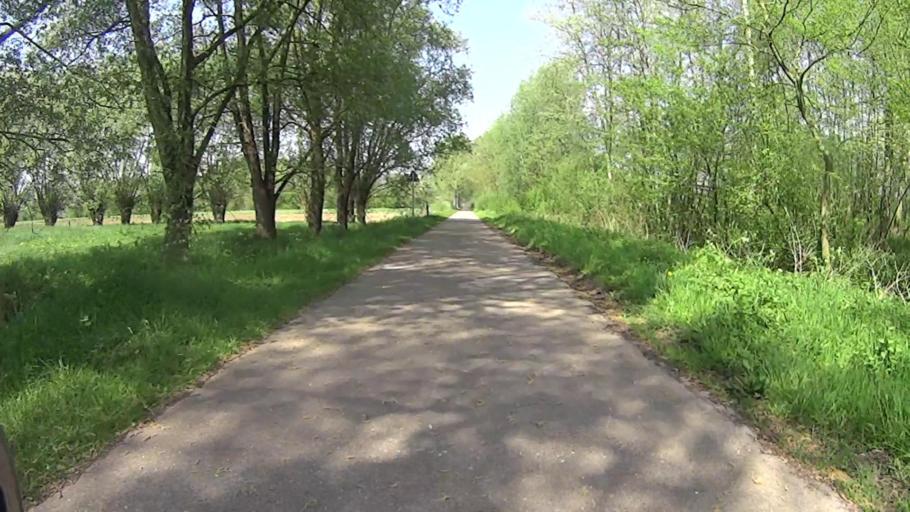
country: BE
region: Flanders
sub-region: Provincie Antwerpen
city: Sint-Amands
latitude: 51.0567
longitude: 4.2221
